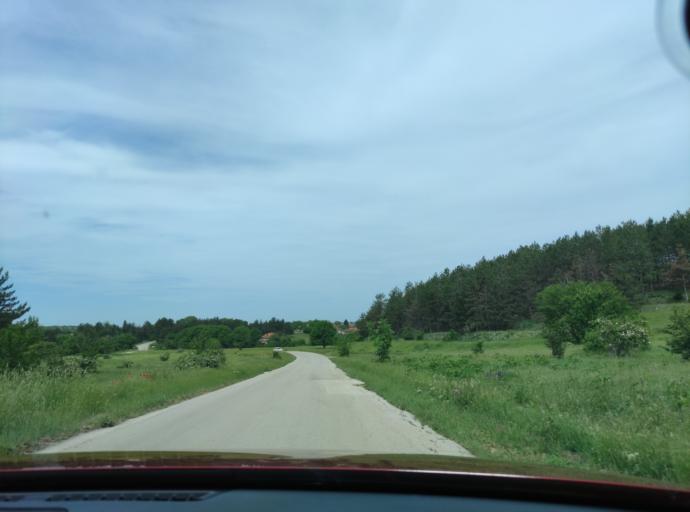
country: BG
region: Pleven
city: Iskur
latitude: 43.5354
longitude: 24.2943
